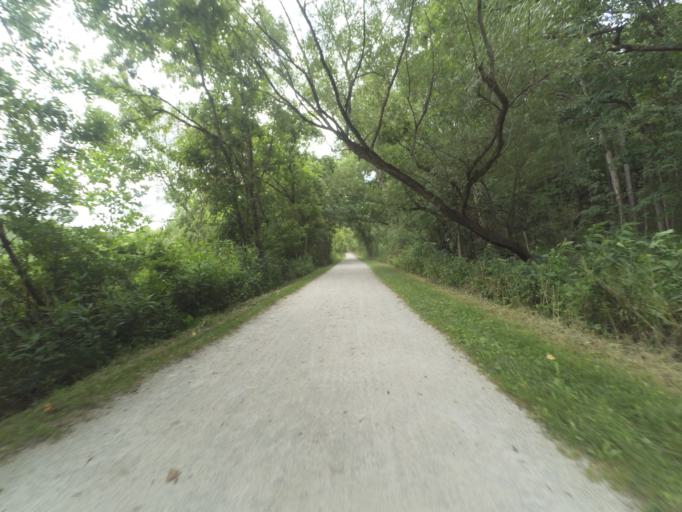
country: US
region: Ohio
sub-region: Cuyahoga County
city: Brecksville
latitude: 41.3089
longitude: -81.5802
